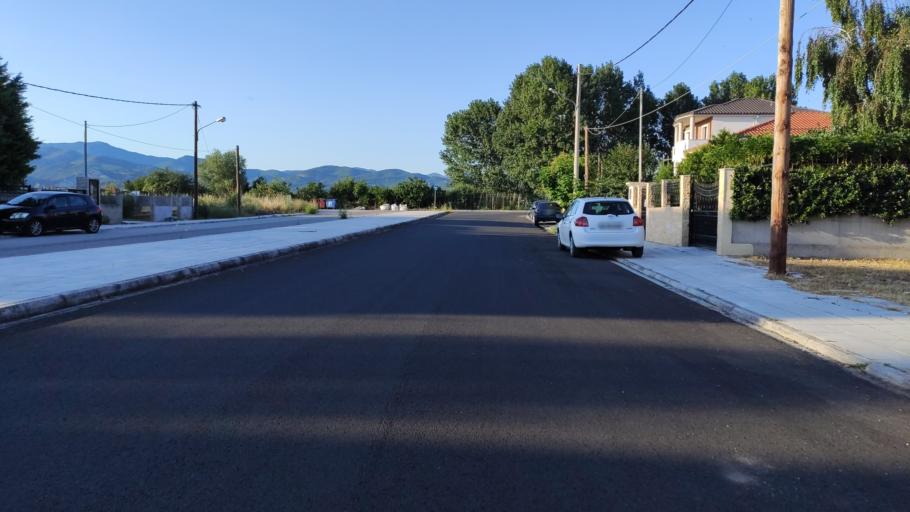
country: GR
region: East Macedonia and Thrace
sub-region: Nomos Rodopis
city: Komotini
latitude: 41.1318
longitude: 25.3977
